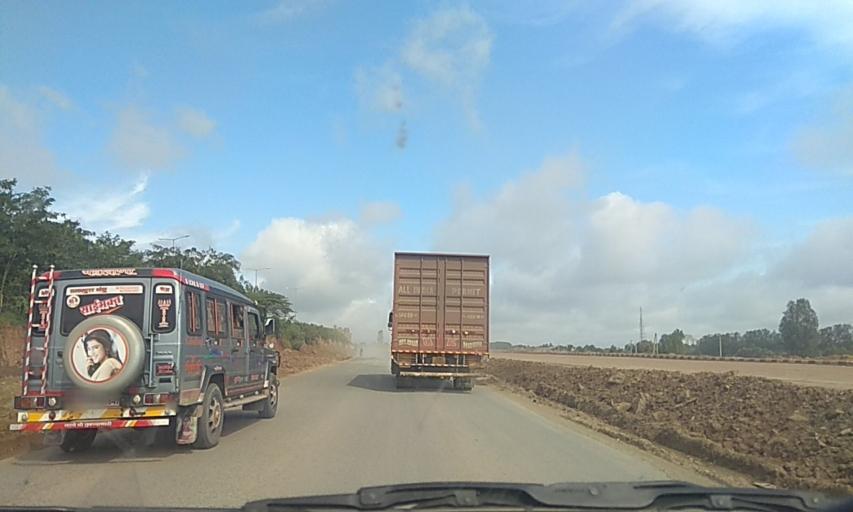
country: IN
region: Karnataka
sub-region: Haveri
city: Shiggaon
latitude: 15.0338
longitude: 75.1776
